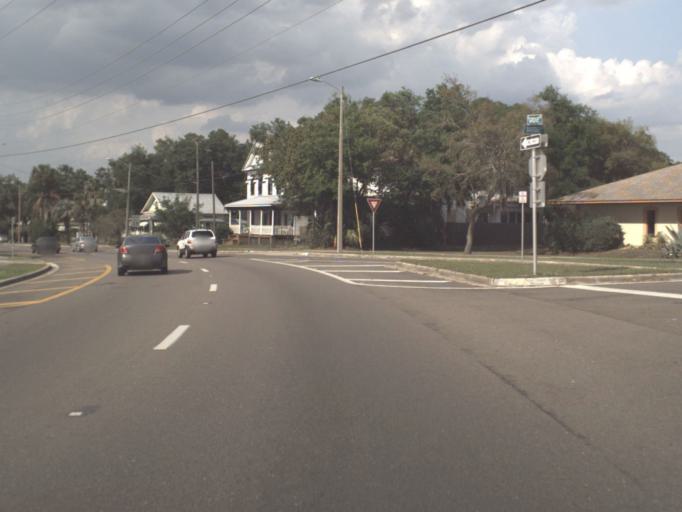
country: US
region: Florida
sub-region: Lake County
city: Eustis
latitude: 28.8464
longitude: -81.6838
